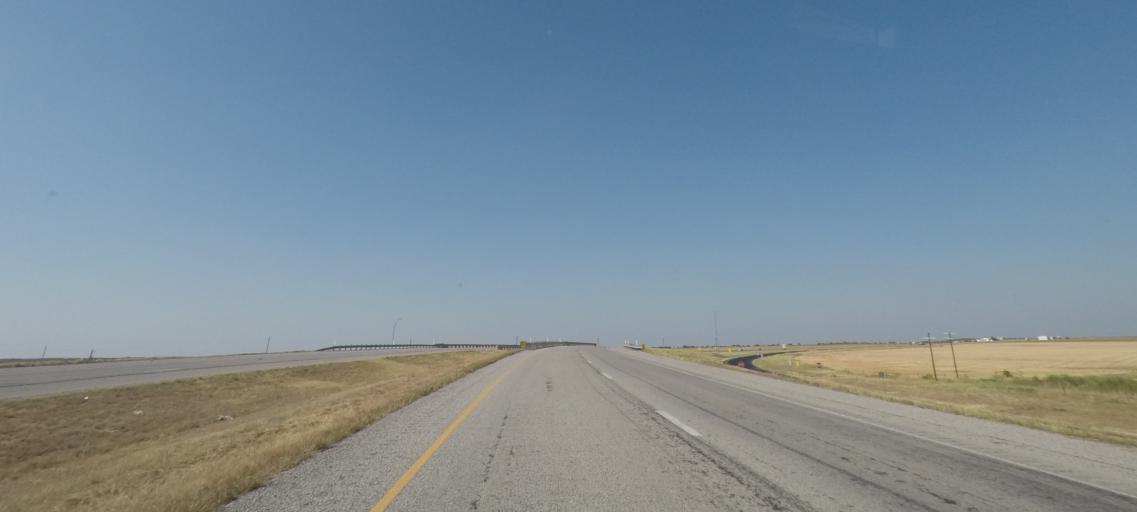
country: US
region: Texas
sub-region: Baylor County
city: Seymour
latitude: 33.6139
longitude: -99.2431
